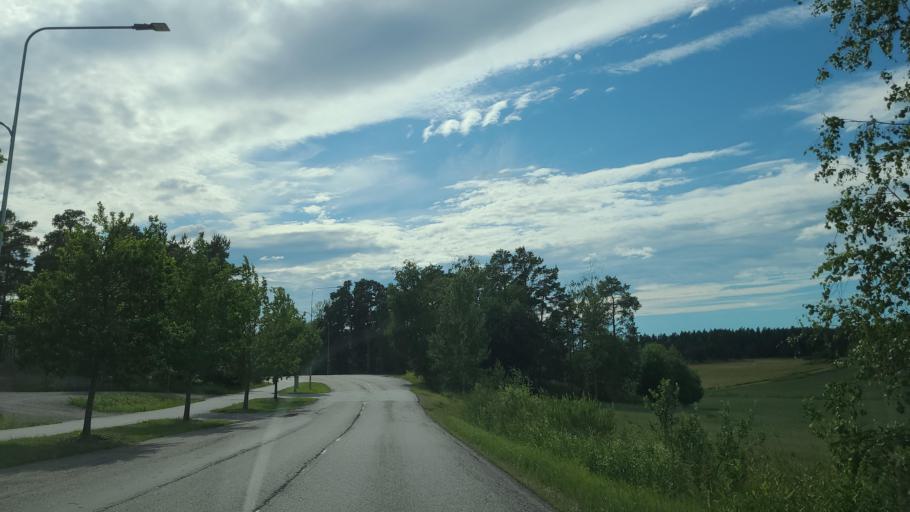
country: FI
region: Varsinais-Suomi
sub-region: Turku
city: Naantali
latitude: 60.4623
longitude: 21.9880
